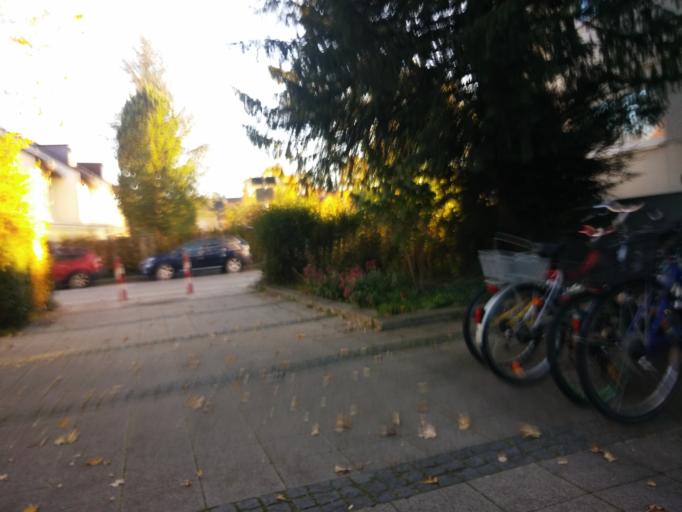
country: DE
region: Bavaria
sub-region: Upper Bavaria
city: Haar
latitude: 48.1057
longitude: 11.7268
